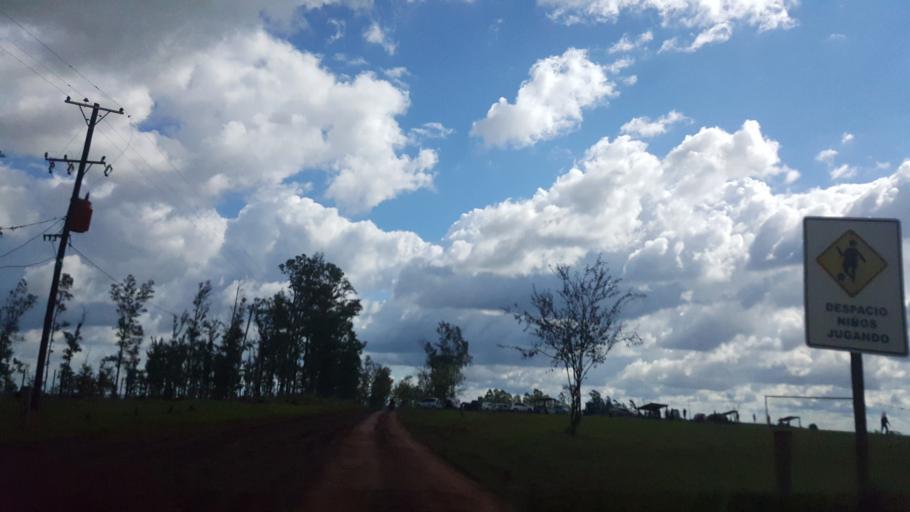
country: AR
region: Misiones
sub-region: Departamento de Capital
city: Posadas
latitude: -27.4188
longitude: -56.0019
